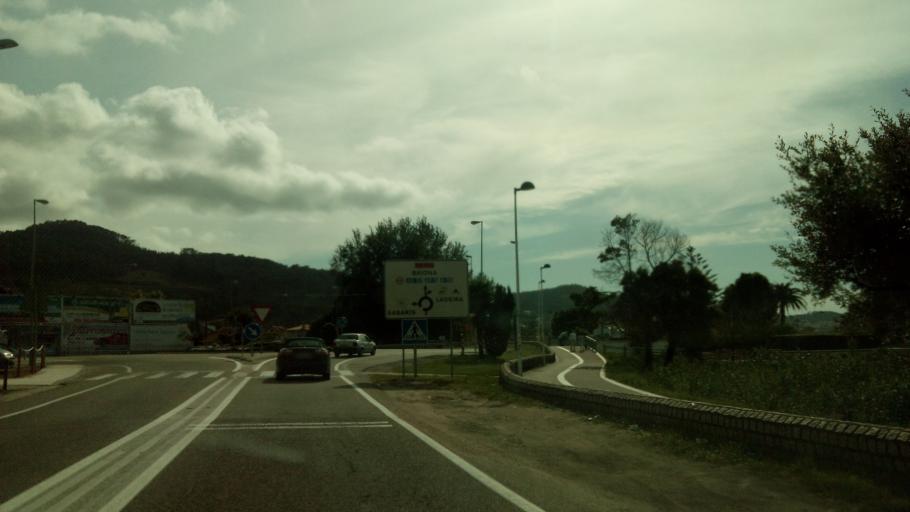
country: ES
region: Galicia
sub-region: Provincia de Pontevedra
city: Baiona
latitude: 42.1126
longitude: -8.8211
